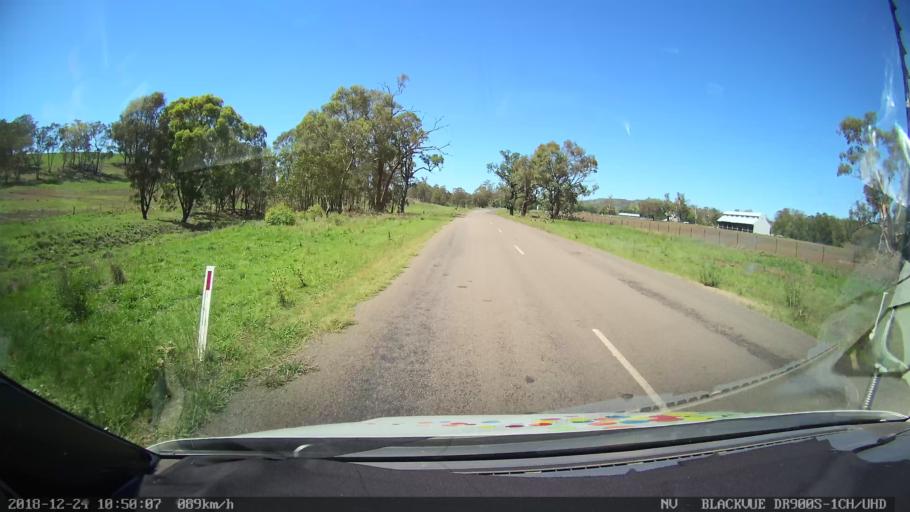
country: AU
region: New South Wales
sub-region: Upper Hunter Shire
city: Merriwa
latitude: -31.9560
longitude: 150.4247
